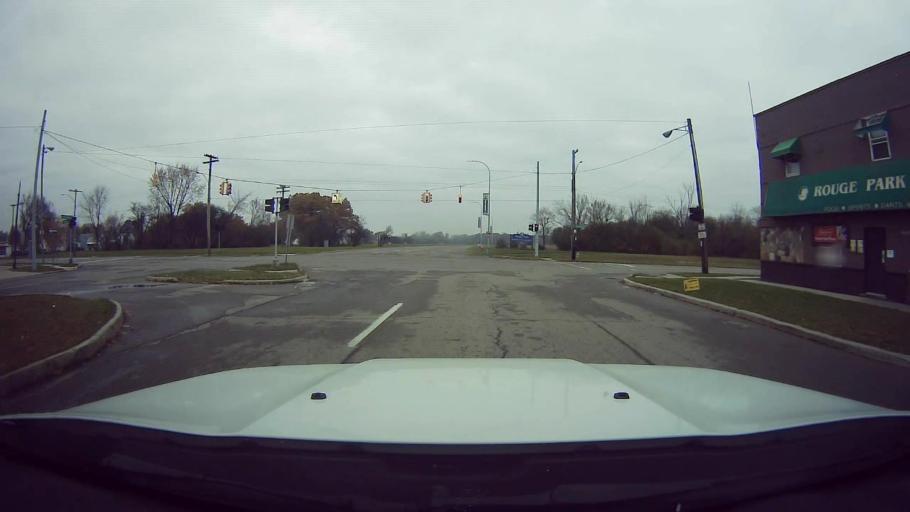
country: US
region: Michigan
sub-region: Wayne County
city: Dearborn Heights
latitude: 42.3418
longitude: -83.2520
